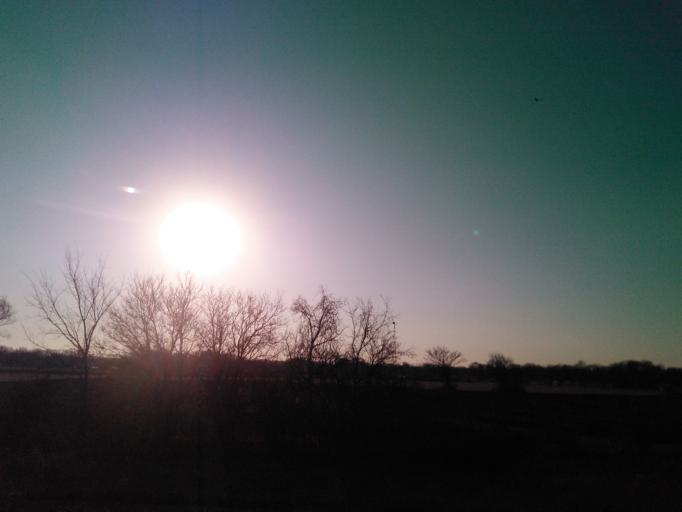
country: US
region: Illinois
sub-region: Saint Clair County
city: Centreville
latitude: 38.5608
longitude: -90.1375
